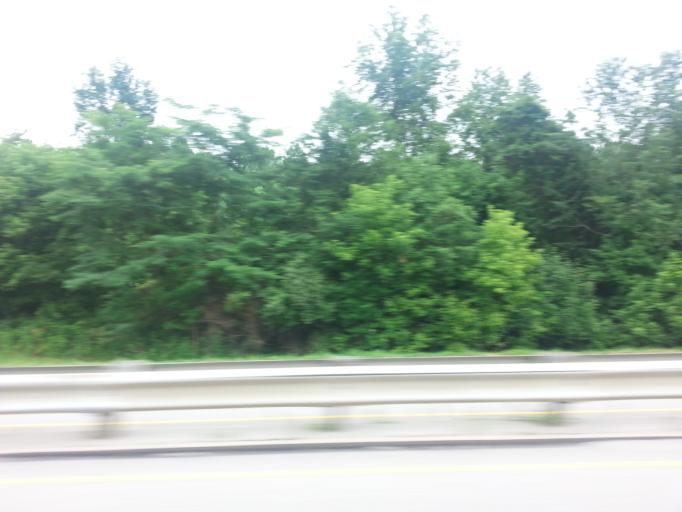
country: US
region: Ohio
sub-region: Brown County
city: Ripley
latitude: 38.7661
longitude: -83.8145
